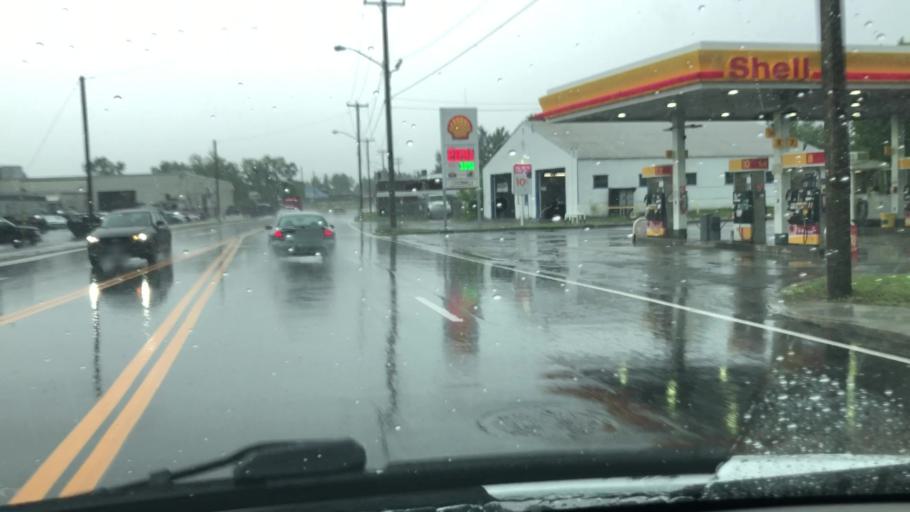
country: US
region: Massachusetts
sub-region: Berkshire County
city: Dalton
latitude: 42.4638
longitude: -73.2063
